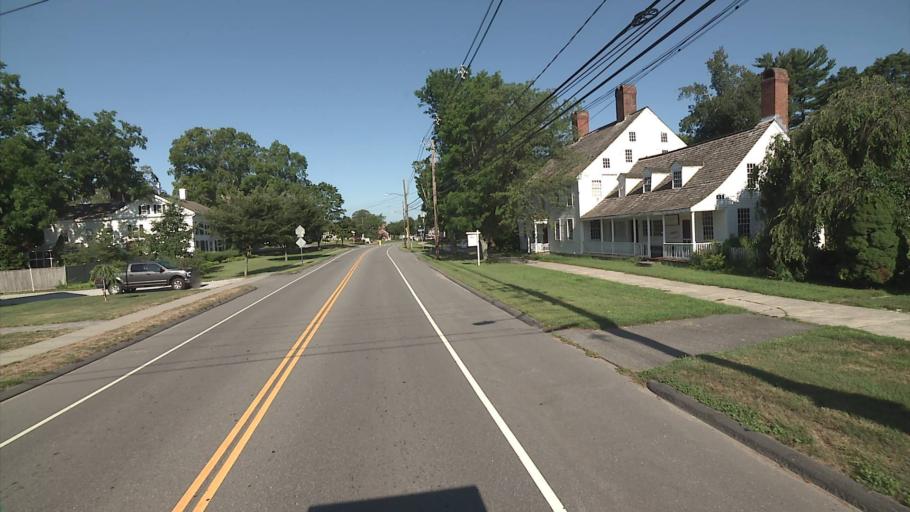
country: US
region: Connecticut
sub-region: Middlesex County
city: Clinton
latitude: 41.2776
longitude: -72.5218
